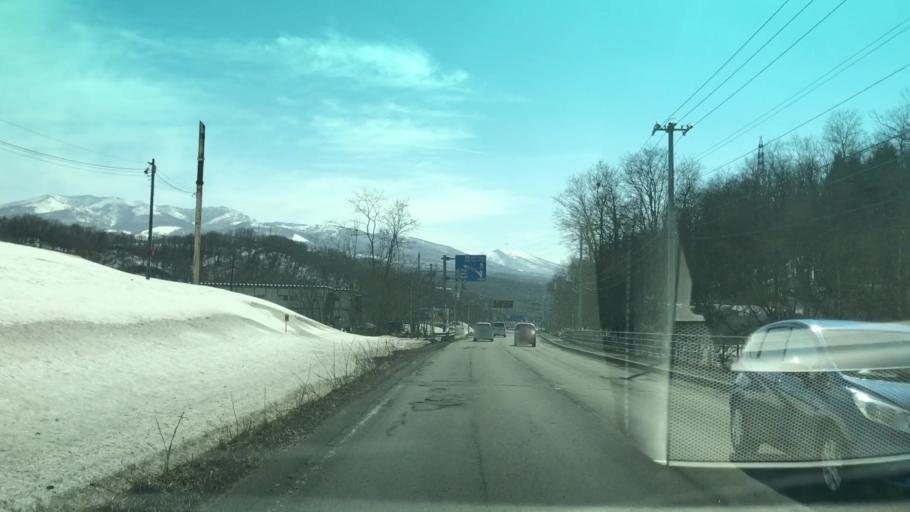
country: JP
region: Hokkaido
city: Iwanai
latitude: 42.9874
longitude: 140.6586
